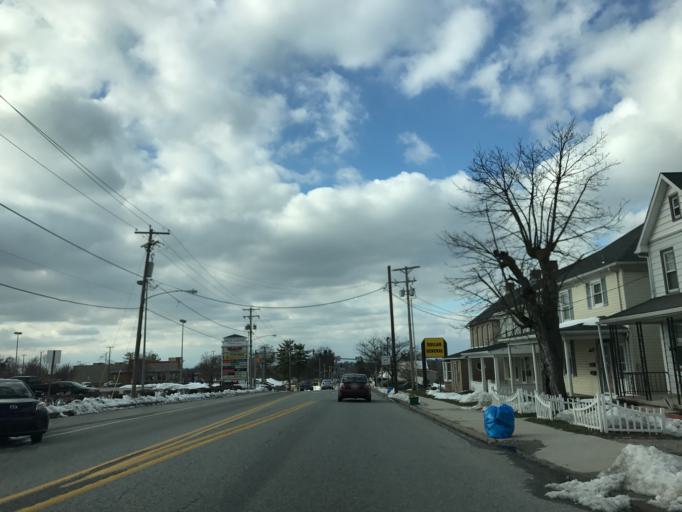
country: US
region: Pennsylvania
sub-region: York County
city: Parkville
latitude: 39.7867
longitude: -76.9681
